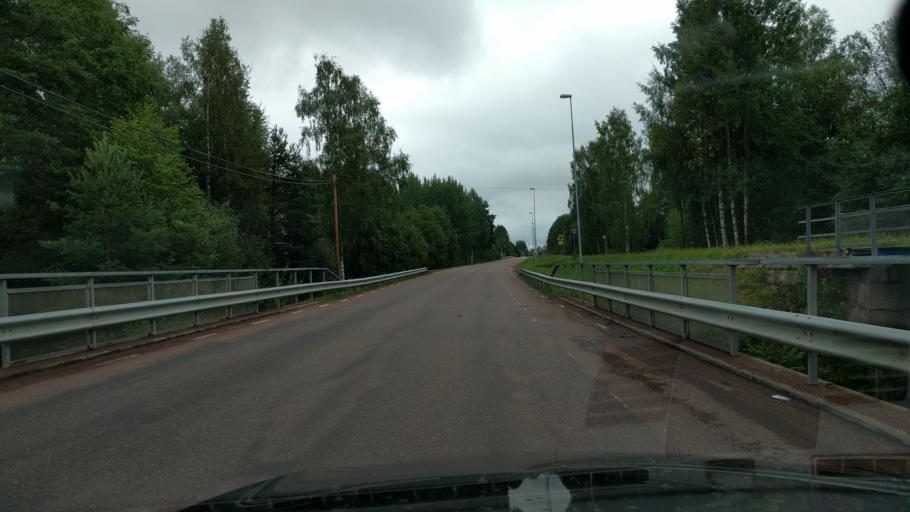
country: SE
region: Dalarna
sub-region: Mora Kommun
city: Mora
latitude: 61.0069
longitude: 14.5185
